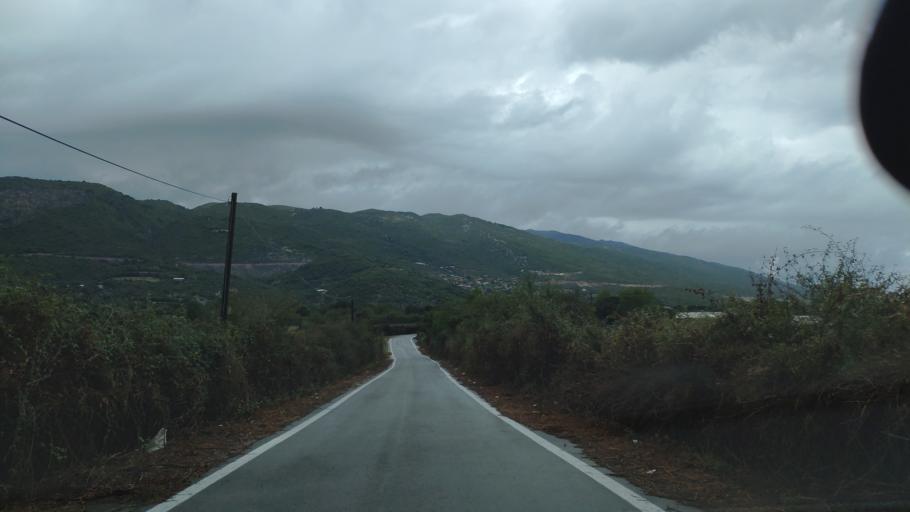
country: GR
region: Central Greece
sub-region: Nomos Evrytanias
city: Kerasochori
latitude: 39.1025
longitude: 21.4299
